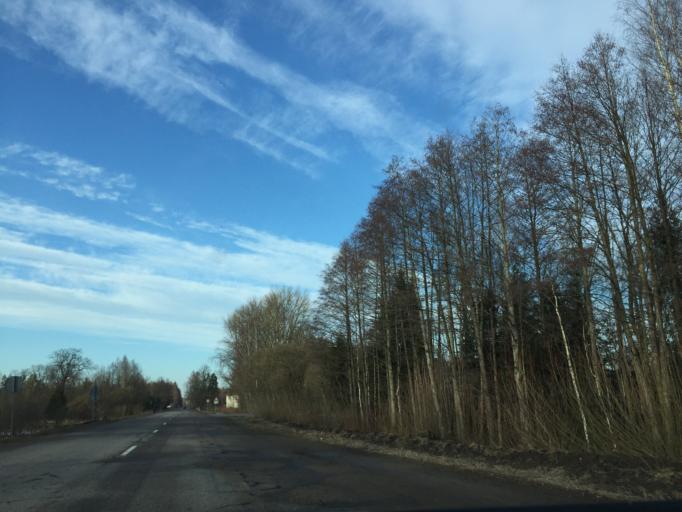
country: LV
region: Kekava
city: Balozi
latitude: 56.7333
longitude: 24.1095
